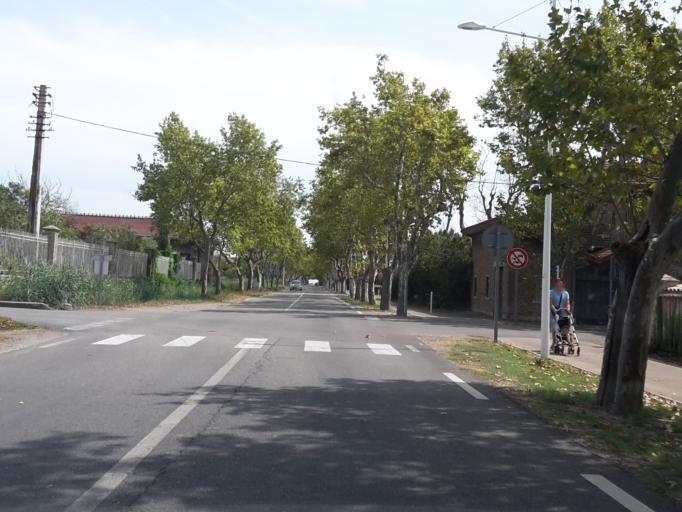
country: FR
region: Provence-Alpes-Cote d'Azur
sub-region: Departement des Bouches-du-Rhone
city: Port-Saint-Louis-du-Rhone
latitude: 43.4182
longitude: 4.7352
